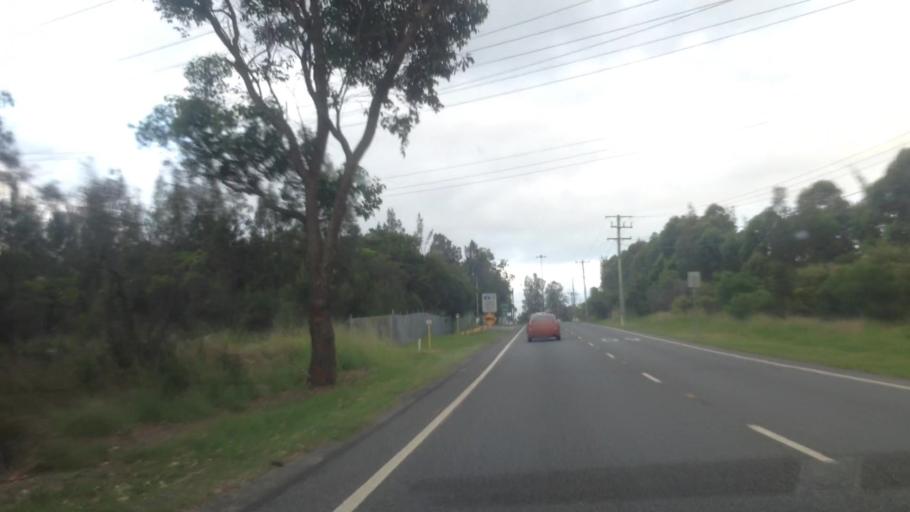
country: AU
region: New South Wales
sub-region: Lake Macquarie Shire
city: Dora Creek
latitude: -33.1139
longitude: 151.4748
